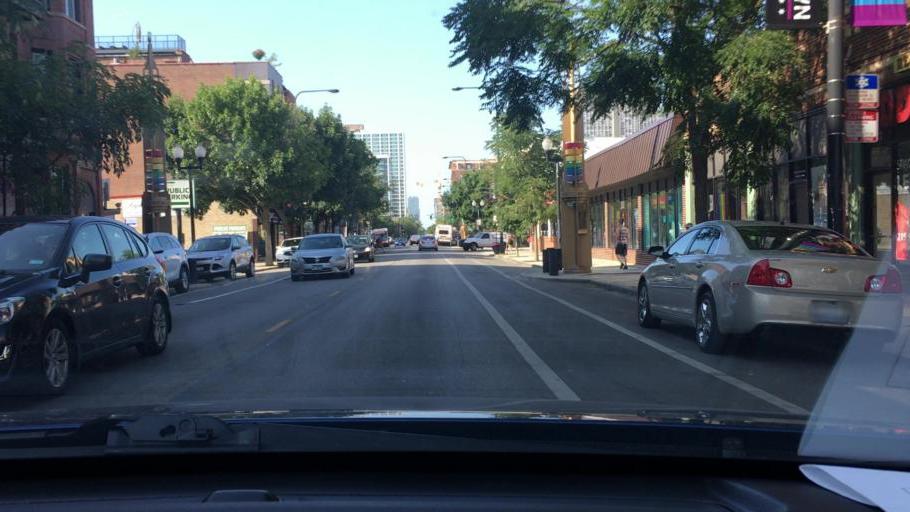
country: US
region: Illinois
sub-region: Cook County
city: Chicago
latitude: 41.9456
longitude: -87.6494
